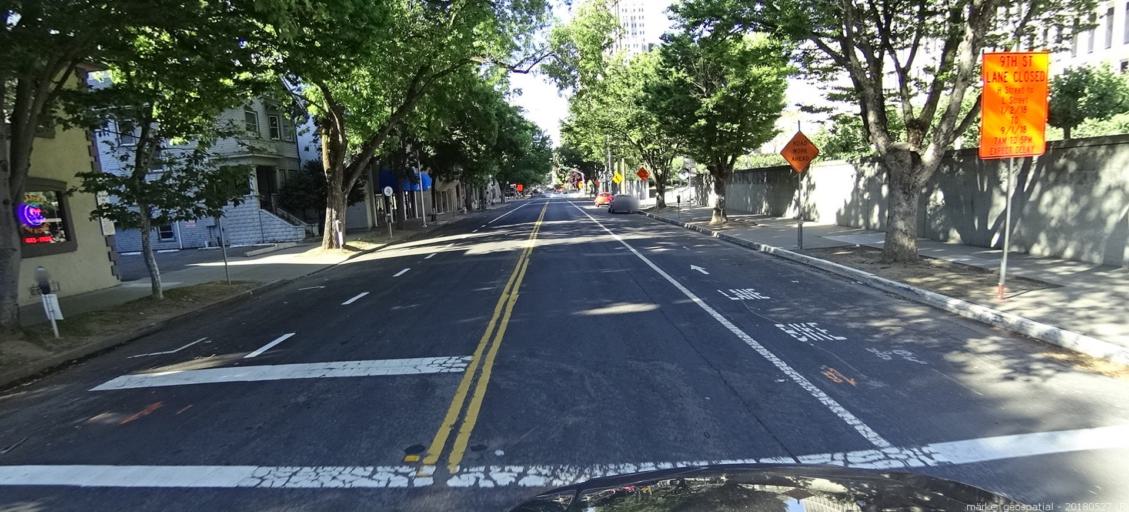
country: US
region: California
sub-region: Sacramento County
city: Sacramento
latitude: 38.5839
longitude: -121.4934
